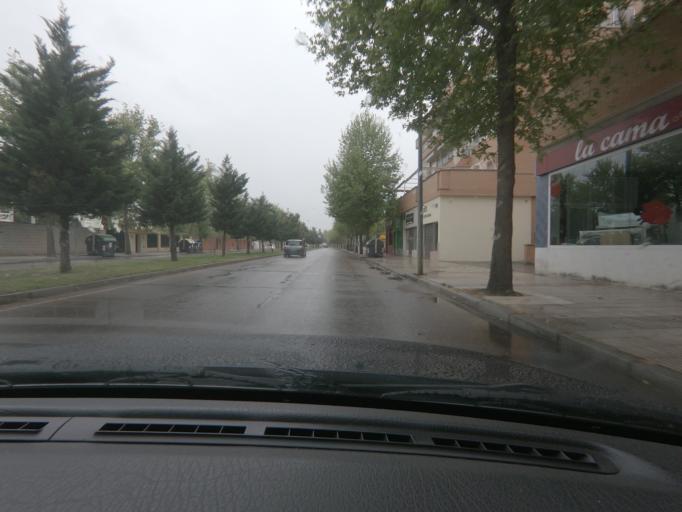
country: ES
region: Extremadura
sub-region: Provincia de Badajoz
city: Badajoz
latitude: 38.8646
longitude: -6.9729
